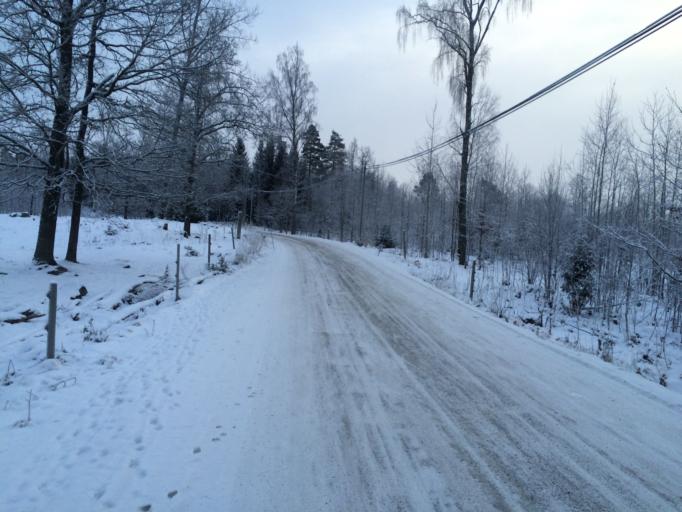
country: SE
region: Uppsala
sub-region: Enkopings Kommun
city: Orsundsbro
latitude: 59.9097
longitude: 17.1808
